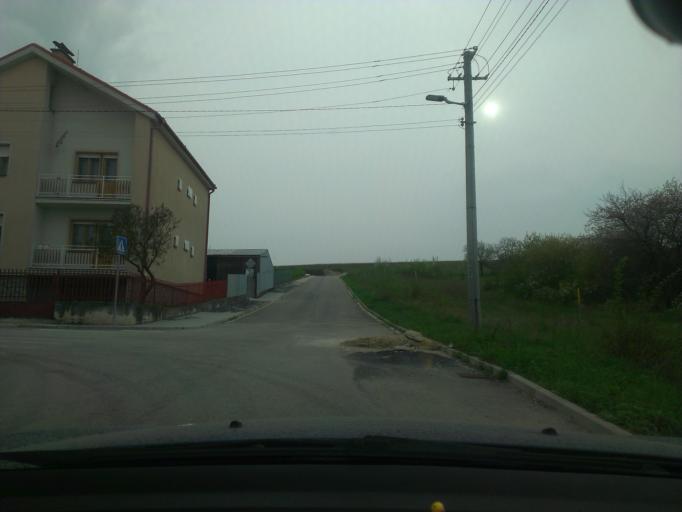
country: SK
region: Trnavsky
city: Vrbove
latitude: 48.6259
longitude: 17.7187
